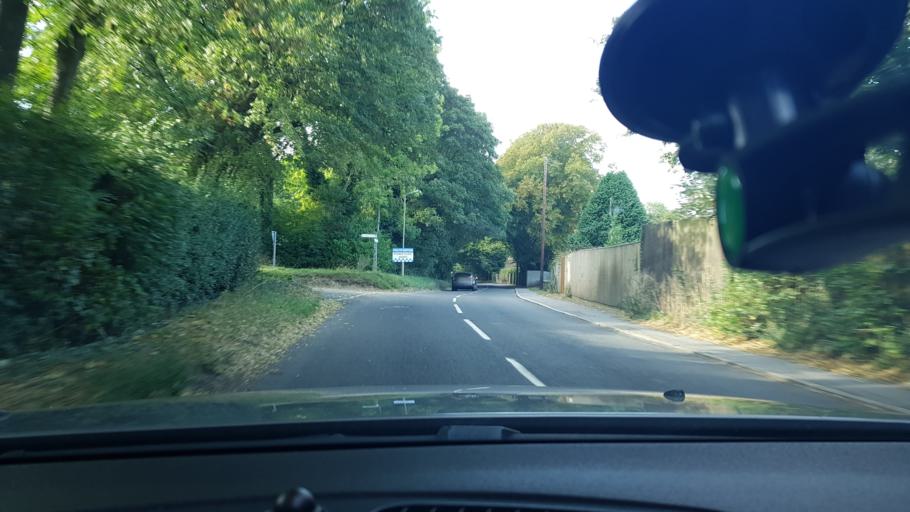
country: GB
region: England
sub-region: West Berkshire
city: Lambourn
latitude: 51.5106
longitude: -1.5347
